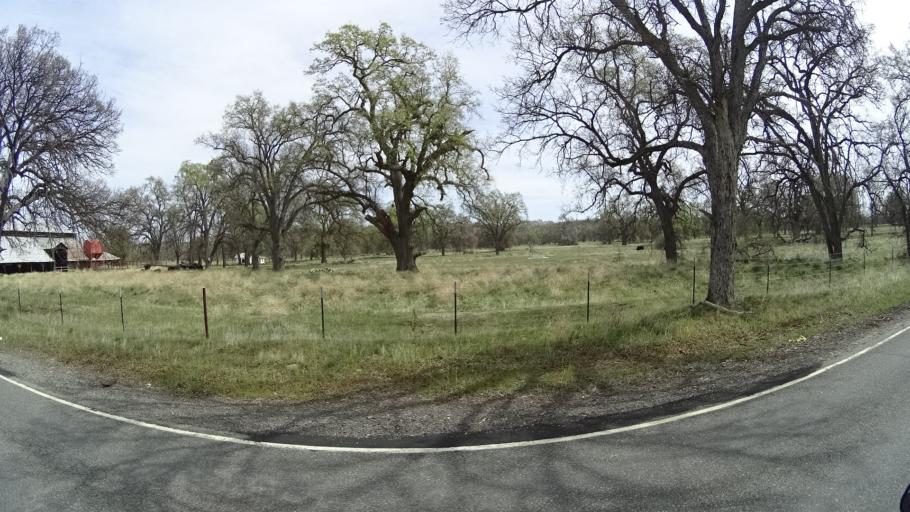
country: US
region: California
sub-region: Colusa County
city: Maxwell
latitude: 39.3965
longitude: -122.5519
